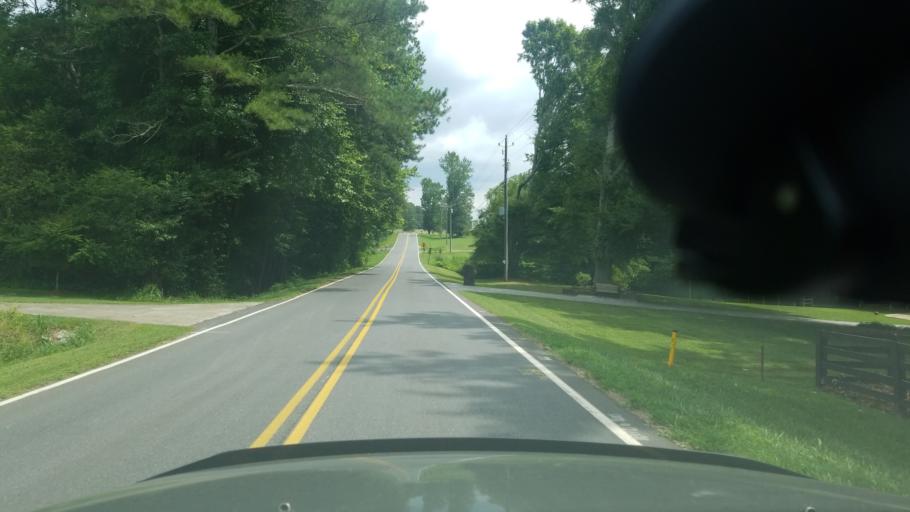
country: US
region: Georgia
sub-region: Dawson County
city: Dawsonville
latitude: 34.3235
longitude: -84.1711
